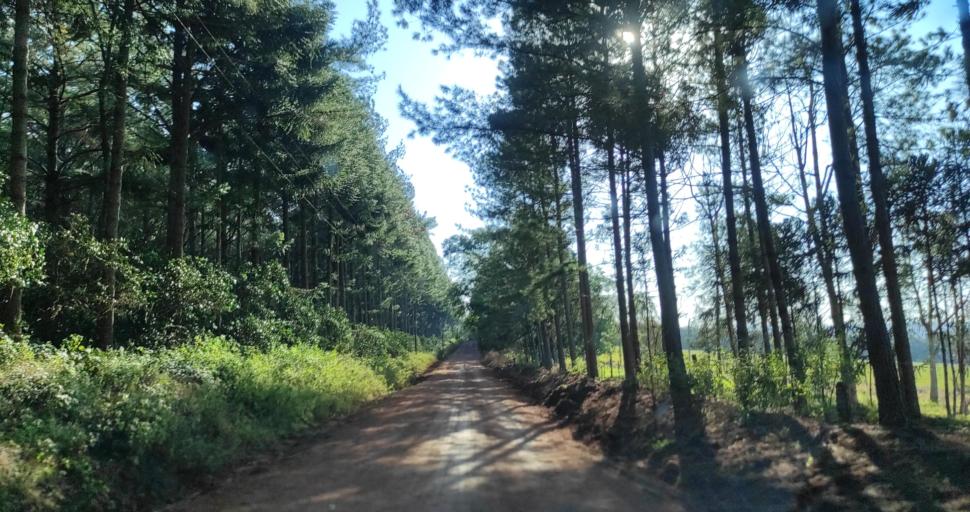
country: AR
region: Misiones
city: Capiovi
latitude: -26.8733
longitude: -55.1192
